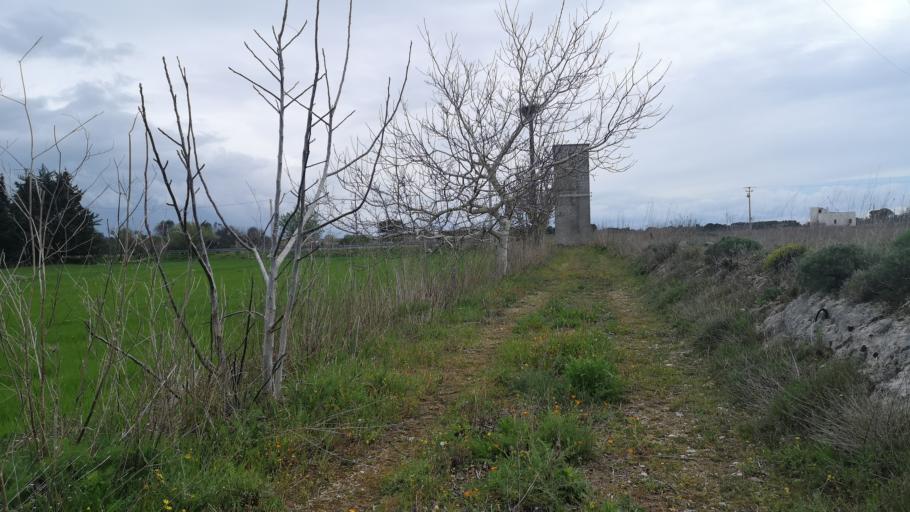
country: IT
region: Apulia
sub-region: Provincia di Lecce
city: Ortelle
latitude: 40.0282
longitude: 18.3805
